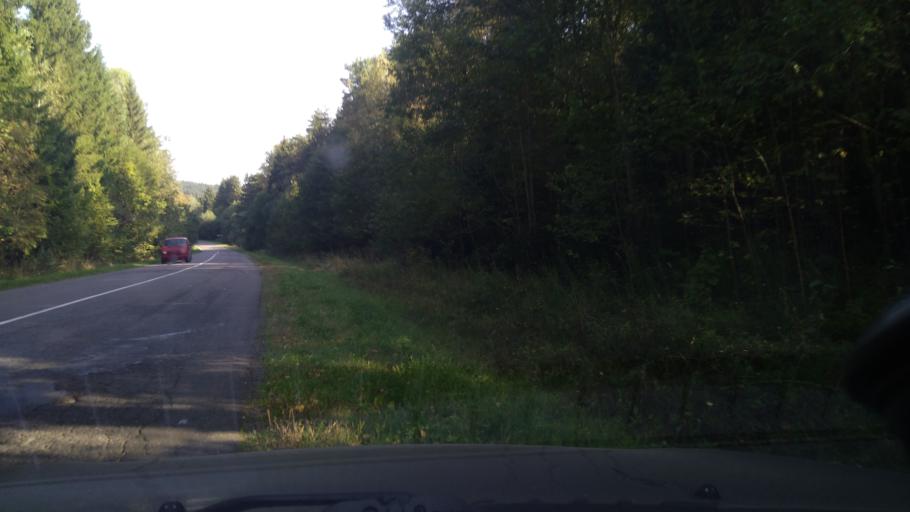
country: BY
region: Minsk
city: Rakaw
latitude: 54.0212
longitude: 27.0524
